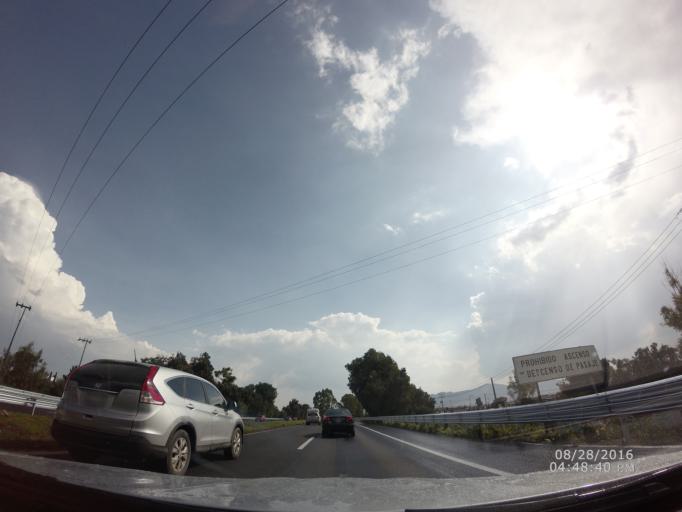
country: MX
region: Mexico
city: Santo Tomas Chiconautla
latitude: 19.6456
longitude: -99.0154
